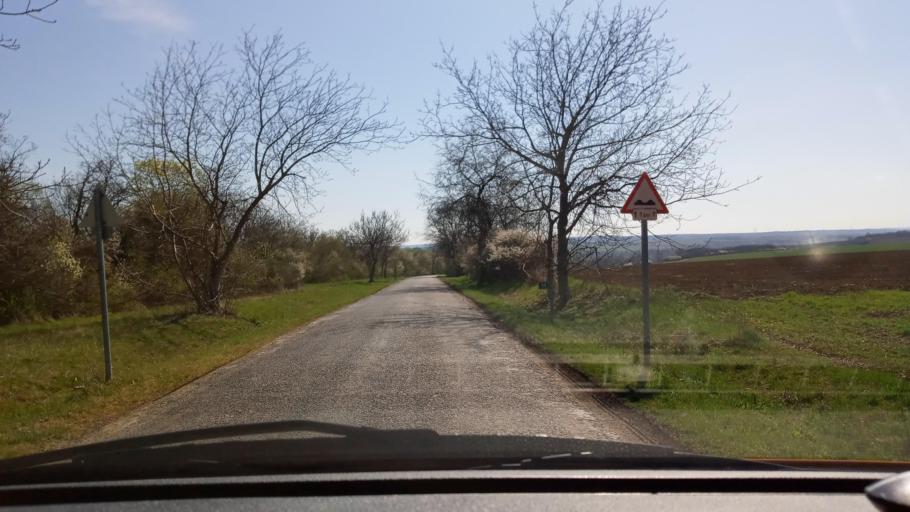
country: HU
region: Baranya
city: Kozarmisleny
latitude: 46.0760
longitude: 18.3525
